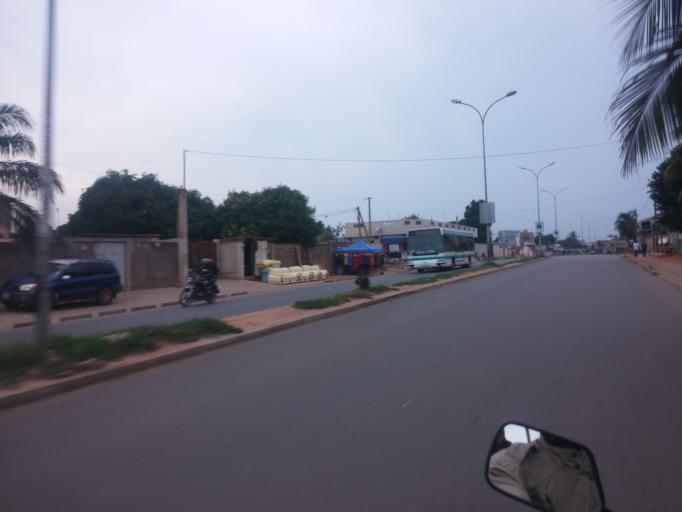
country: TG
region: Maritime
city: Lome
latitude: 6.2029
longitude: 1.1836
